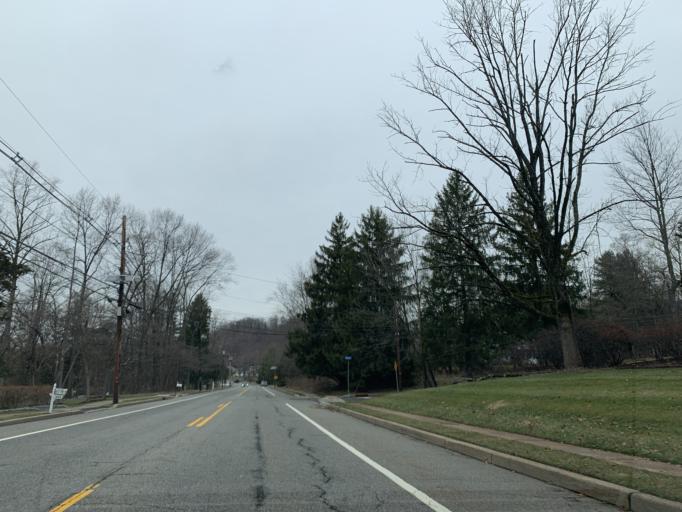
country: US
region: New Jersey
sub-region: Somerset County
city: Martinsville
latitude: 40.6158
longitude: -74.5819
